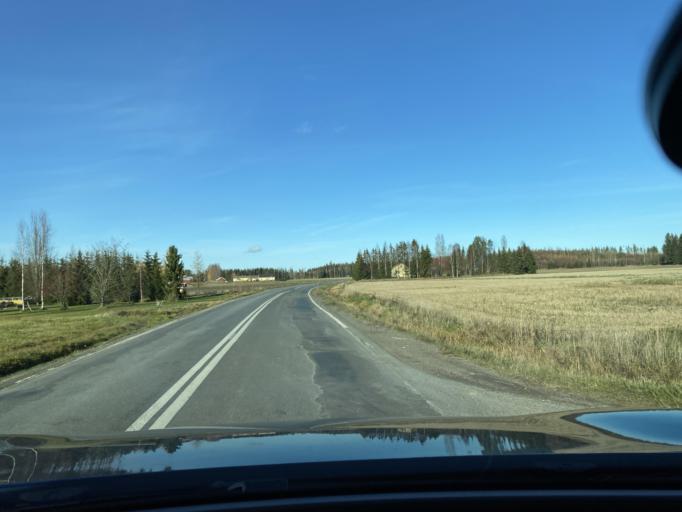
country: FI
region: Haeme
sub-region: Forssa
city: Tammela
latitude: 60.8315
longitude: 23.8401
